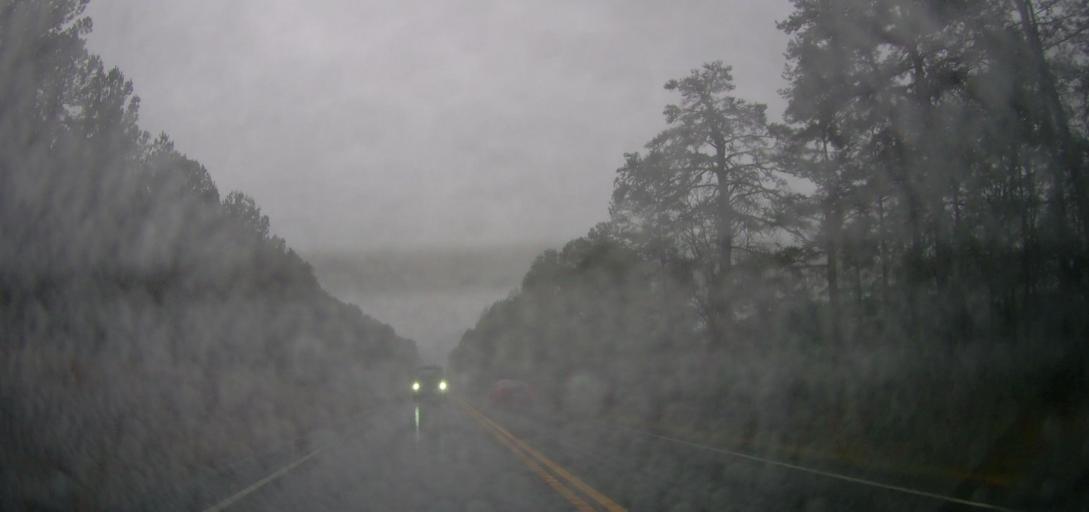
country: US
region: Georgia
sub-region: Putnam County
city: Eatonton
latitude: 33.1974
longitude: -83.4341
